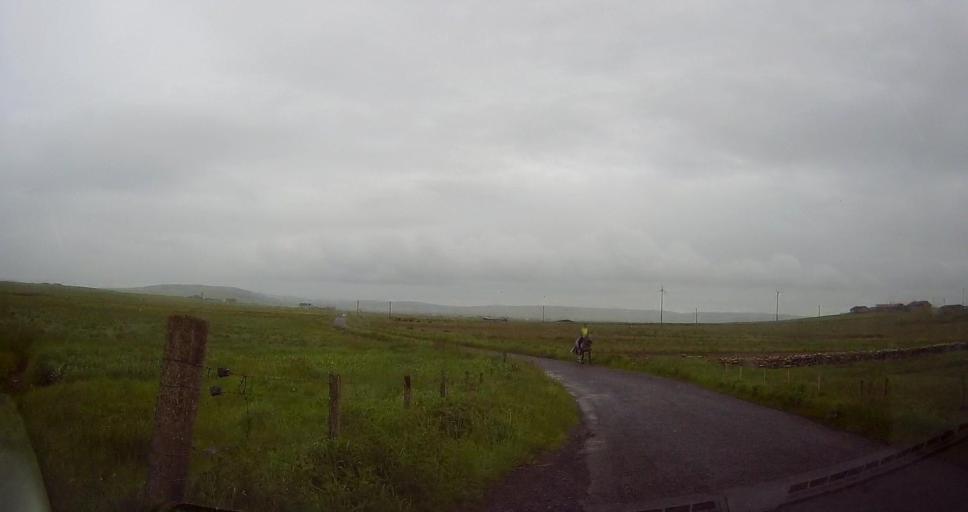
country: GB
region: Scotland
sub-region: Orkney Islands
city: Stromness
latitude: 59.0691
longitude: -3.3032
